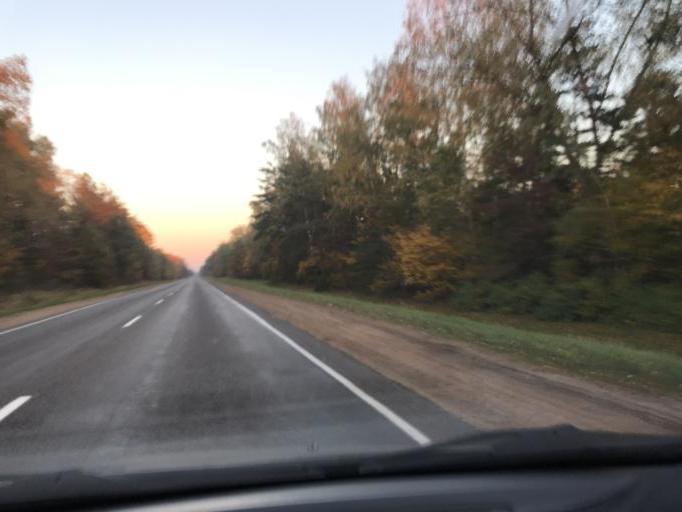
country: BY
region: Mogilev
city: Hlusha
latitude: 53.0935
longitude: 28.9455
